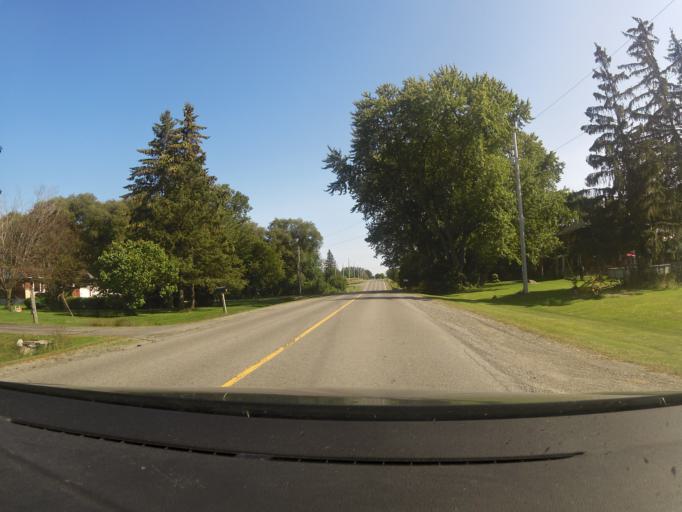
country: CA
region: Ontario
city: Carleton Place
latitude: 45.3482
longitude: -76.0861
